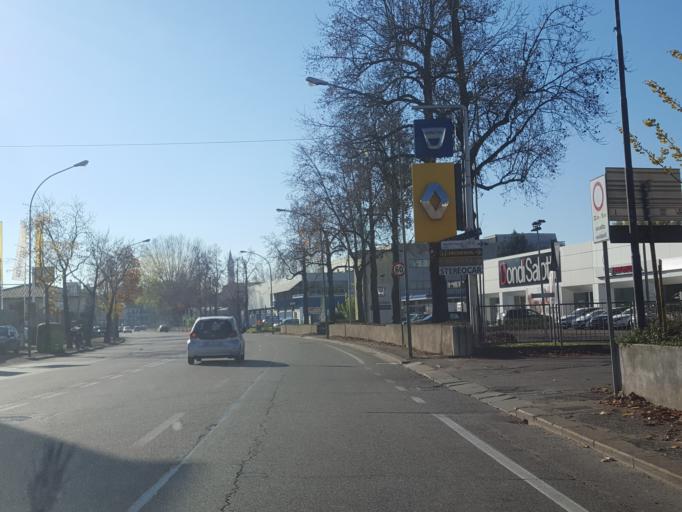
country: IT
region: Veneto
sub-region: Provincia di Verona
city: Verona
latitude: 45.4242
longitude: 10.9913
